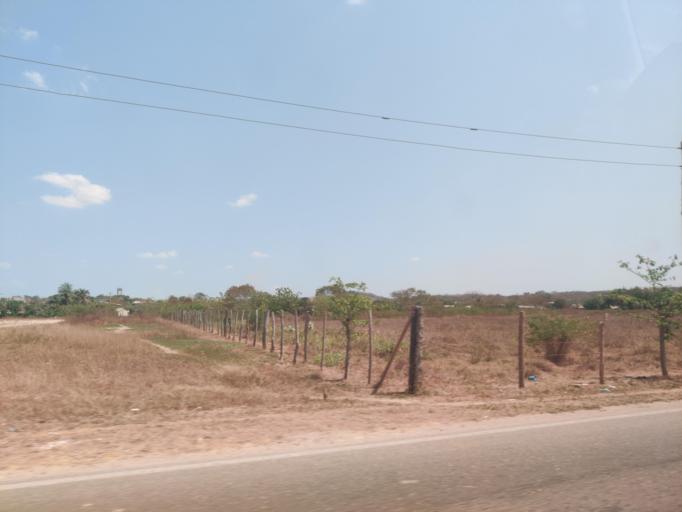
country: CO
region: Bolivar
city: Turbana
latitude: 10.2763
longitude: -75.5140
